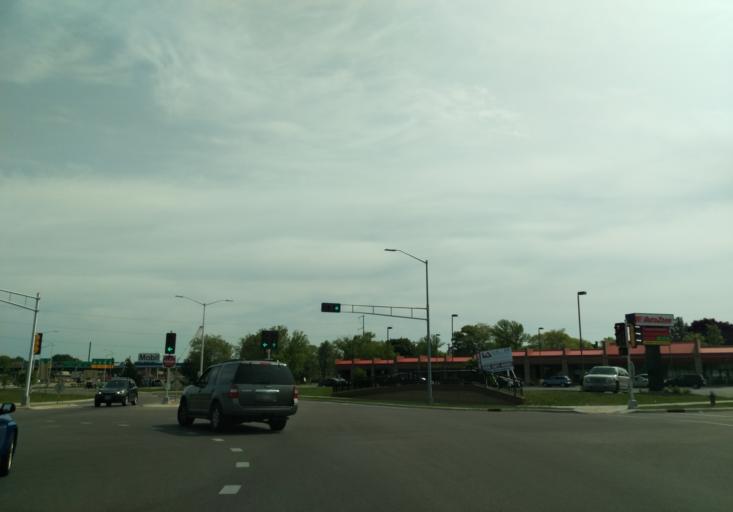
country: US
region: Wisconsin
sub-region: Dane County
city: Shorewood Hills
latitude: 43.0337
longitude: -89.4555
